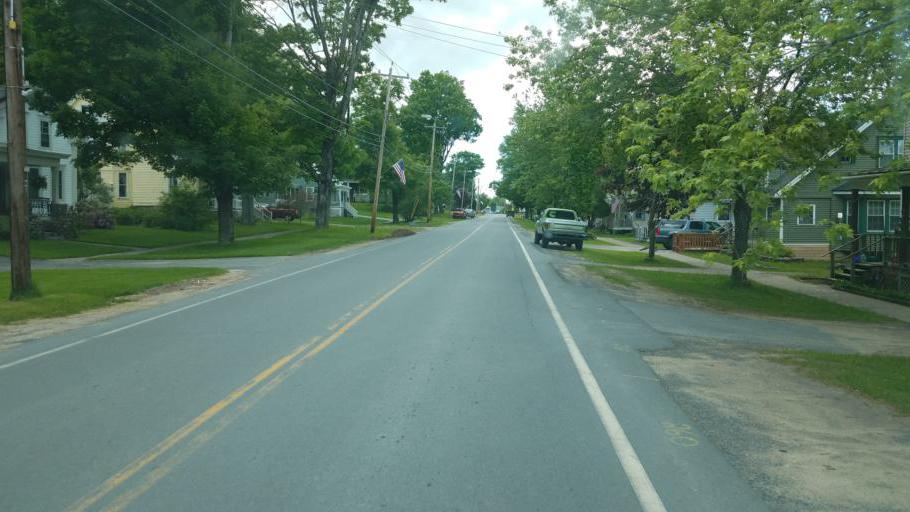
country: US
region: New York
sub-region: Oneida County
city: Boonville
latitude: 43.3289
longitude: -75.1872
